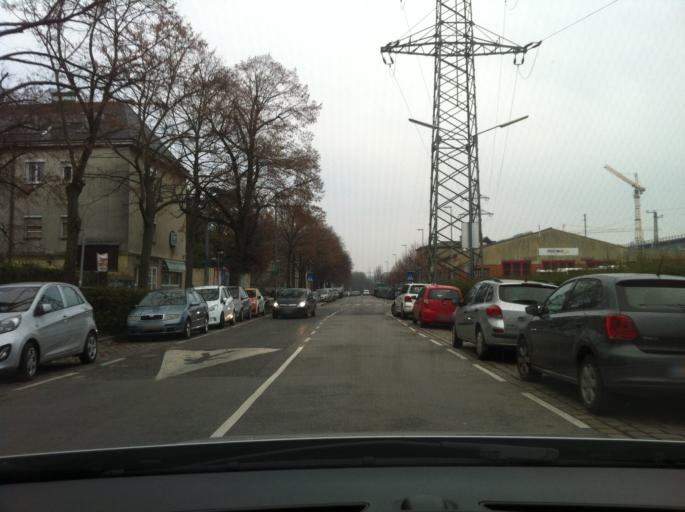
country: AT
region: Lower Austria
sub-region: Politischer Bezirk Modling
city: Perchtoldsdorf
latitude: 48.1981
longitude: 16.2615
